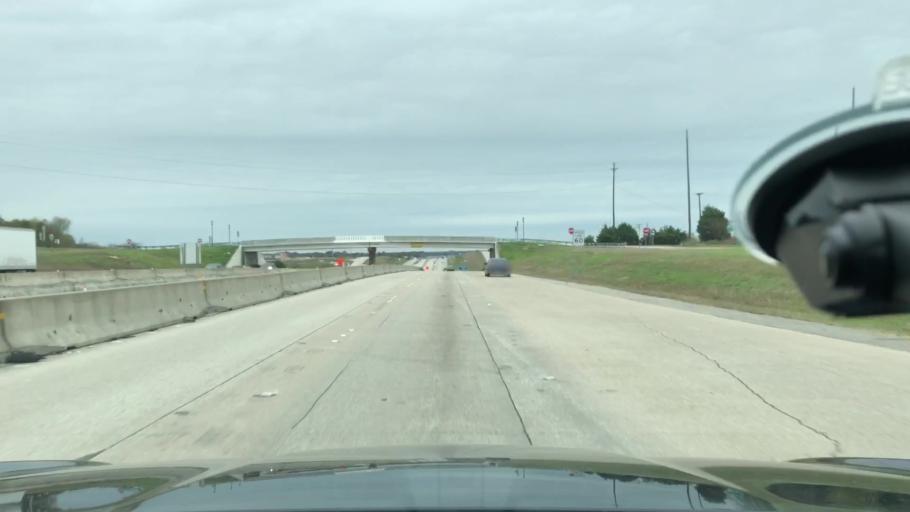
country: US
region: Texas
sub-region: Ellis County
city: Waxahachie
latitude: 32.3772
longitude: -96.8647
